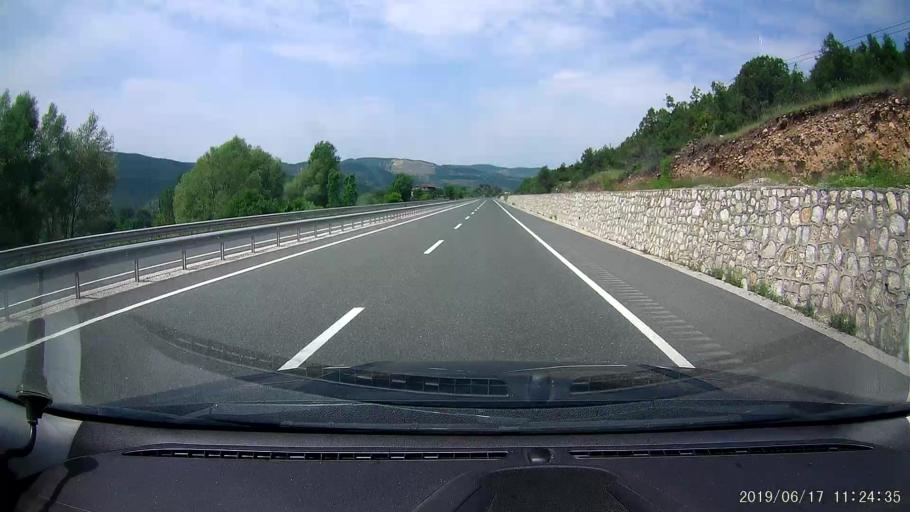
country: TR
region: Cankiri
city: Ilgaz
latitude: 40.8852
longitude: 33.7003
